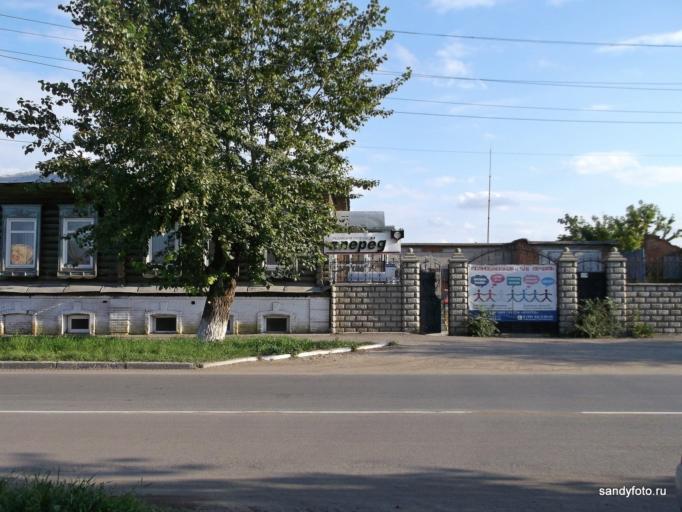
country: RU
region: Chelyabinsk
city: Troitsk
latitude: 54.0854
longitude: 61.5664
